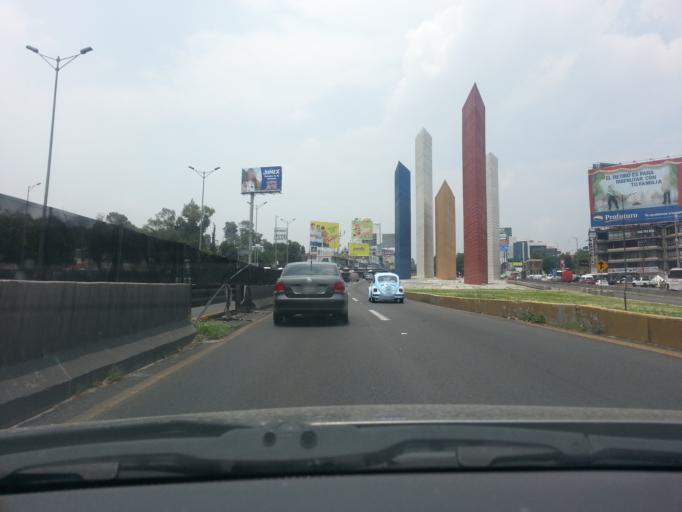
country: MX
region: Mexico
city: Naucalpan de Juarez
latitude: 19.4978
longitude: -99.2369
